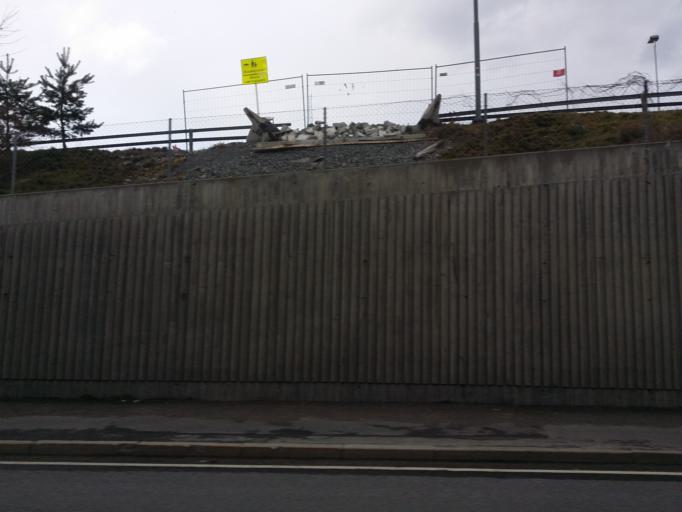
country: NO
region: Oslo
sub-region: Oslo
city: Oslo
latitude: 59.9272
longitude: 10.8090
